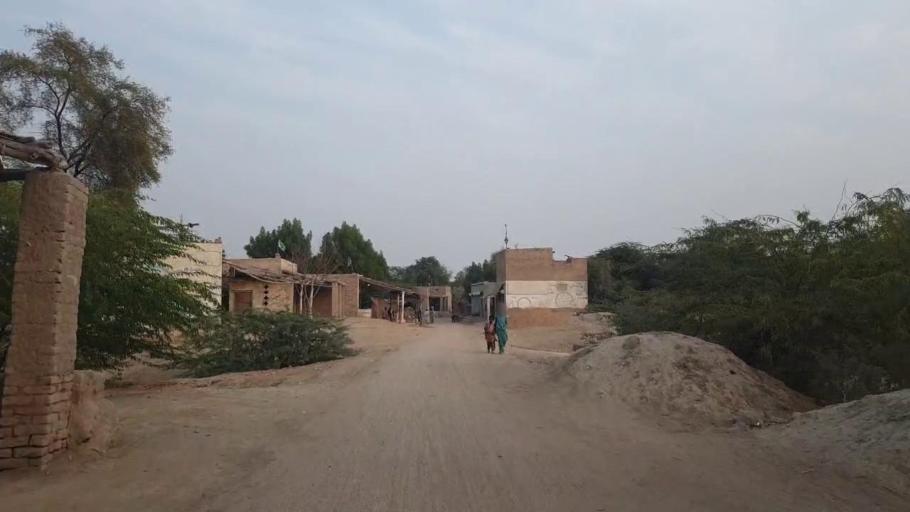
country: PK
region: Sindh
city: Sann
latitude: 26.1720
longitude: 68.0166
